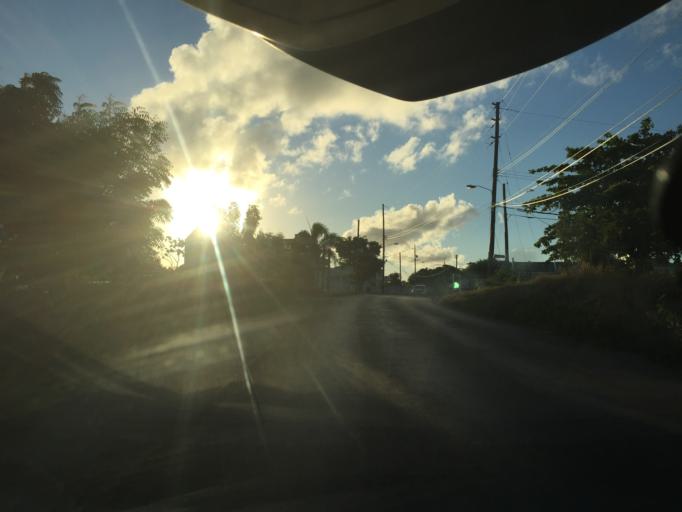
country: BB
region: Christ Church
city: Oistins
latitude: 13.0788
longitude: -59.5076
